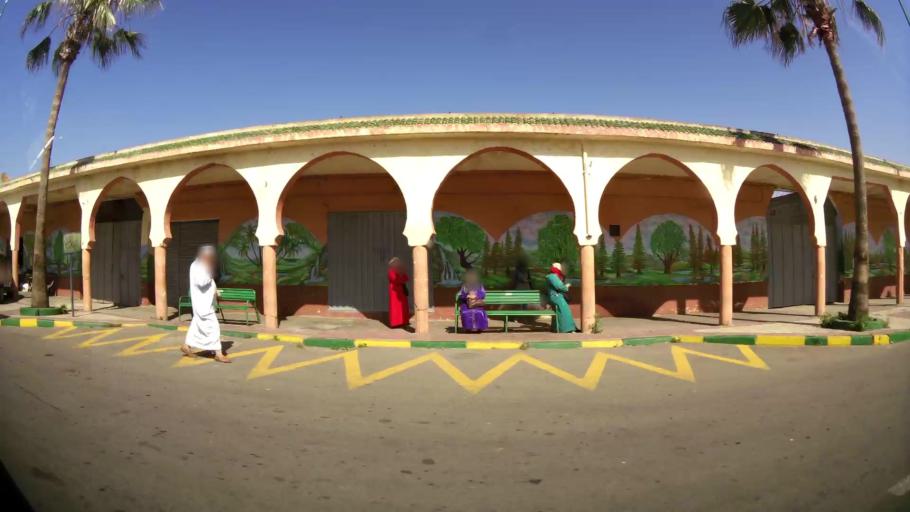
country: MA
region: Souss-Massa-Draa
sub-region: Inezgane-Ait Mellou
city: Inezgane
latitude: 30.3635
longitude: -9.5334
